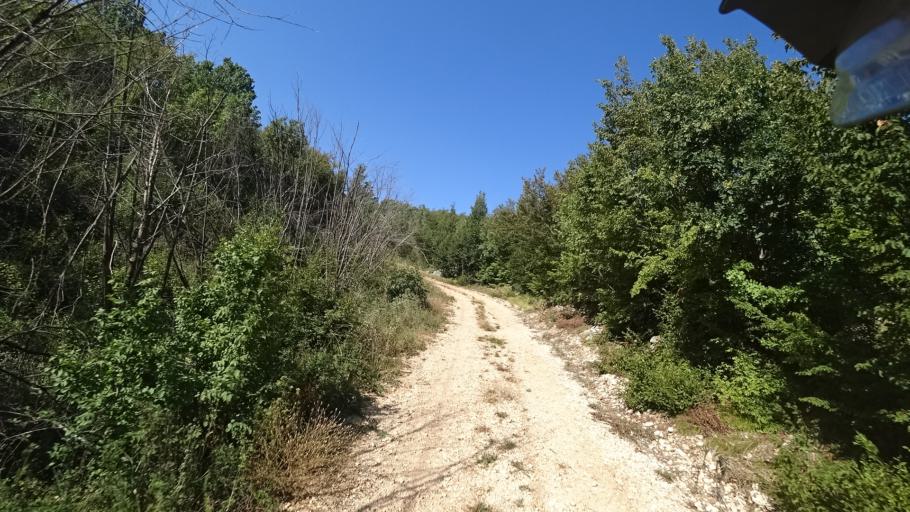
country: HR
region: Sibensko-Kniniska
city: Knin
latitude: 43.9596
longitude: 16.1575
